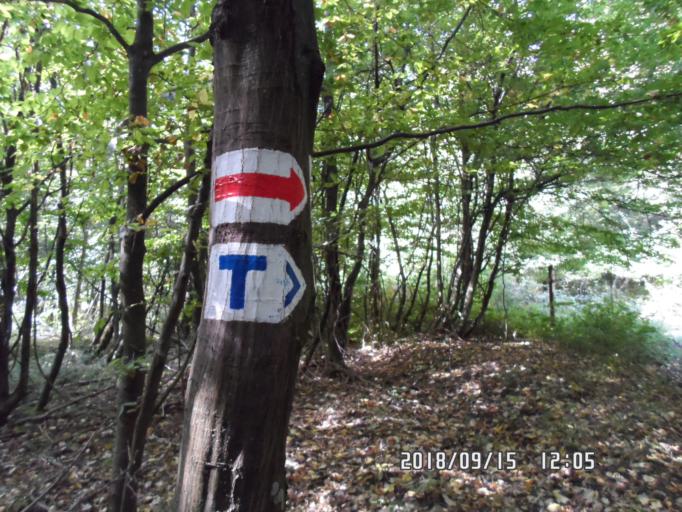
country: HU
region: Veszprem
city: Cseteny
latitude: 47.2489
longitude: 17.9734
